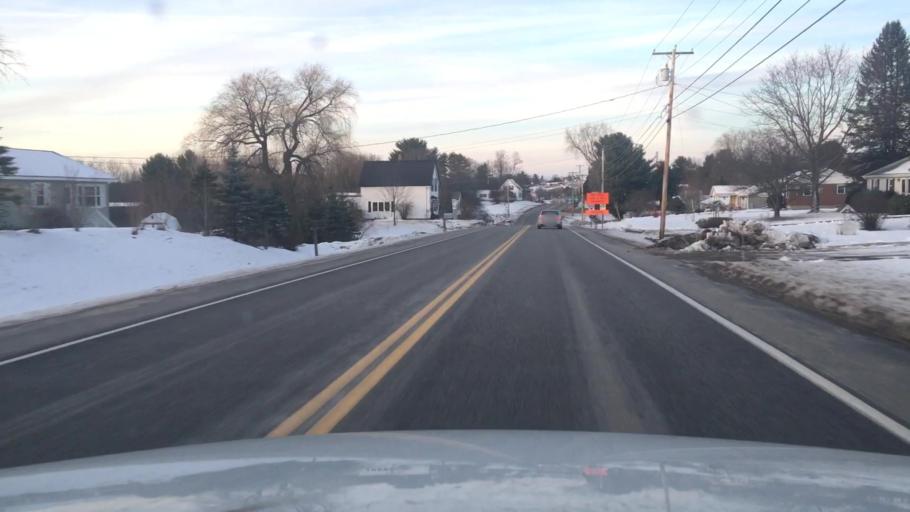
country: US
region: Maine
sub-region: Androscoggin County
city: Sabattus
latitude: 44.0971
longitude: -70.0844
